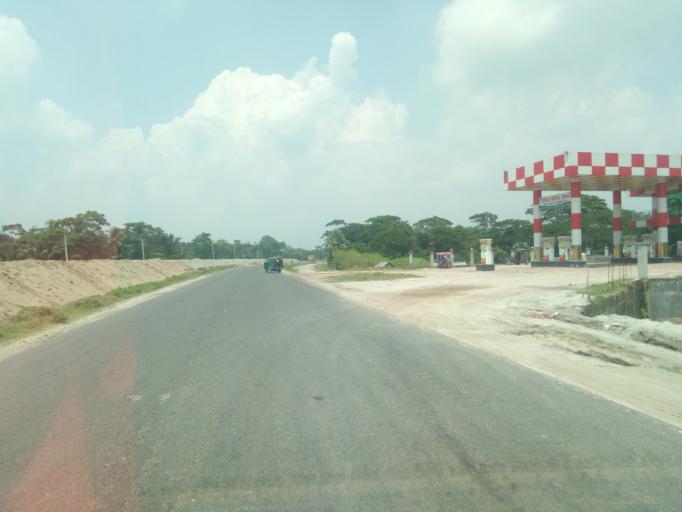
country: BD
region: Dhaka
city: Char Bhadrasan
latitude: 23.3909
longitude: 90.1252
